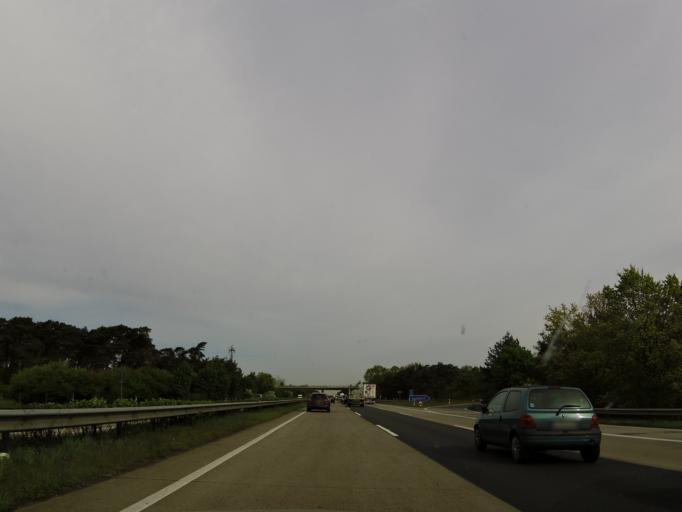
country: DE
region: Lower Saxony
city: Elze
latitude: 52.6074
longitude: 9.7405
